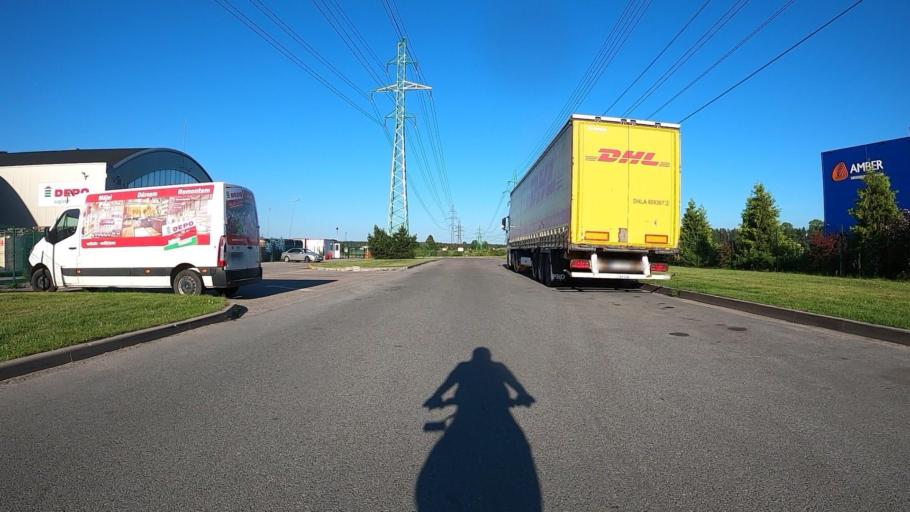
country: LV
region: Stopini
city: Ulbroka
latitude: 56.9295
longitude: 24.2383
